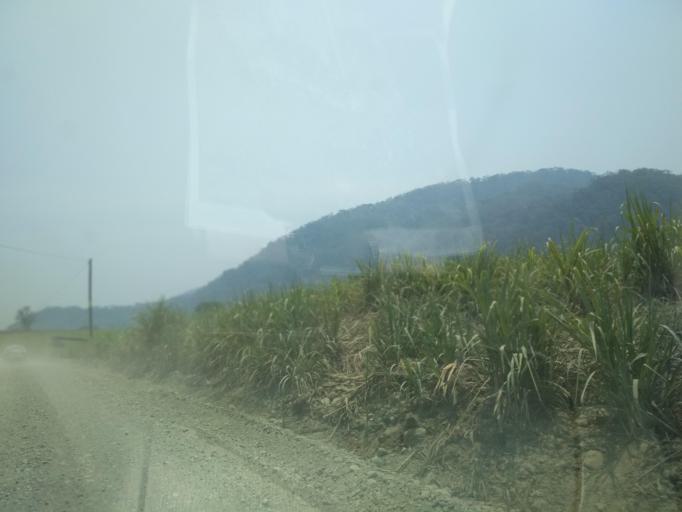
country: MX
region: Veracruz
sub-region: Tezonapa
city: Laguna Chica (Pueblo Nuevo)
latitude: 18.5619
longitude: -96.7237
